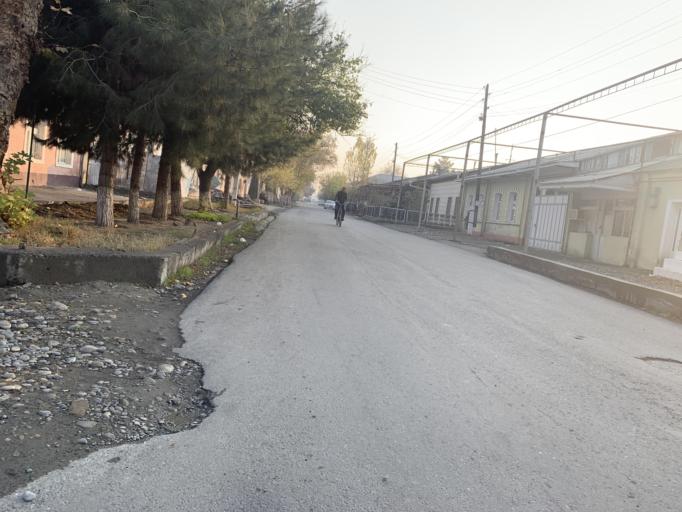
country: UZ
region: Fergana
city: Qo`qon
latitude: 40.5224
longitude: 70.9382
